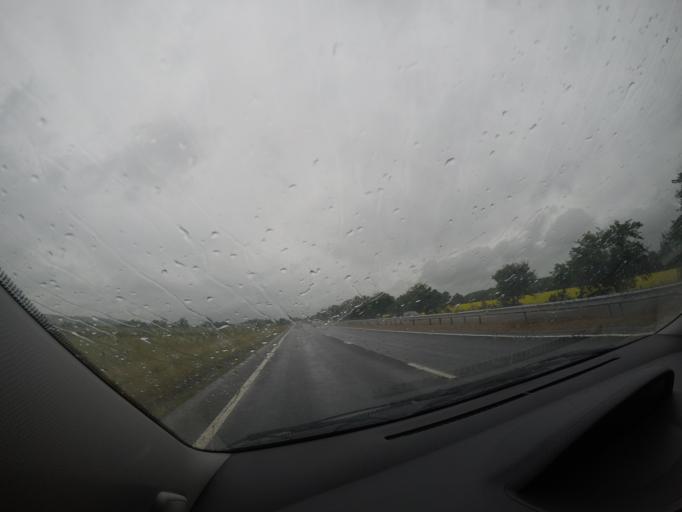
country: GB
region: Scotland
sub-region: Angus
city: Letham
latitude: 56.7188
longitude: -2.7669
